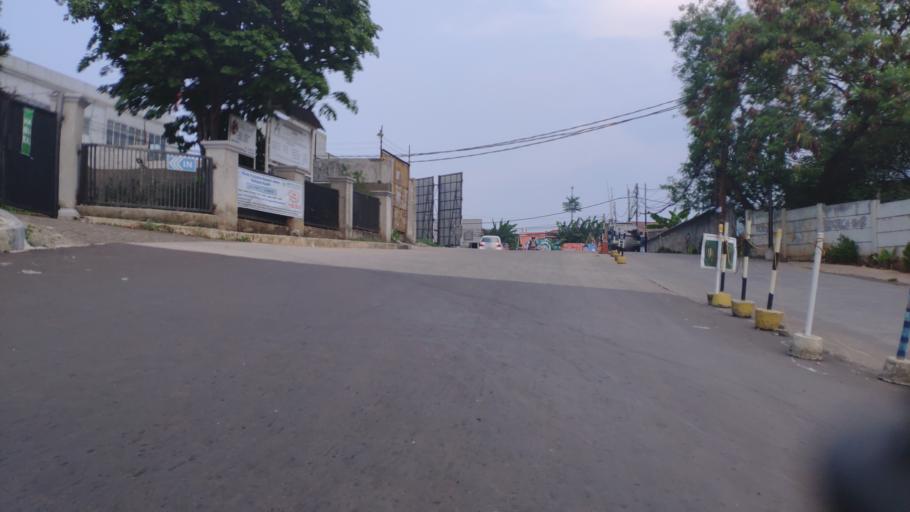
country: ID
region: West Java
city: Pamulang
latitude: -6.3468
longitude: 106.7757
